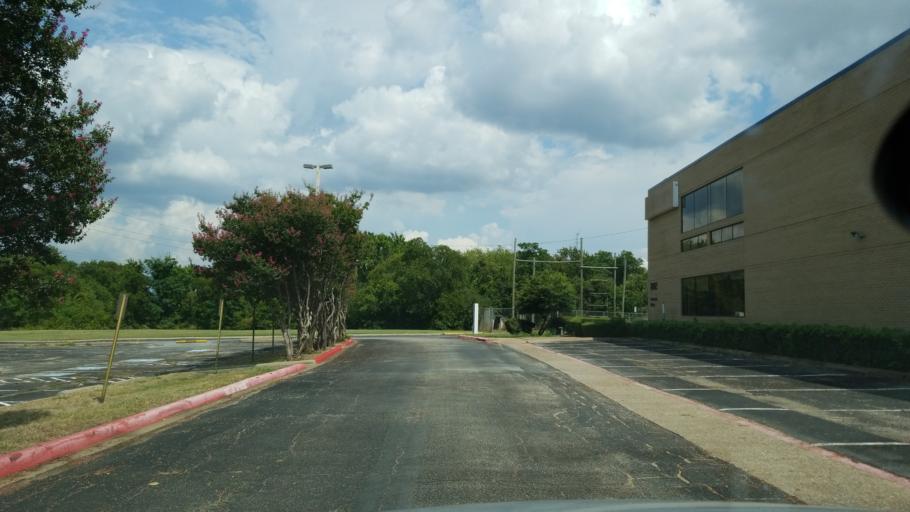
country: US
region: Texas
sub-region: Dallas County
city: Garland
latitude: 32.9138
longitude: -96.6696
